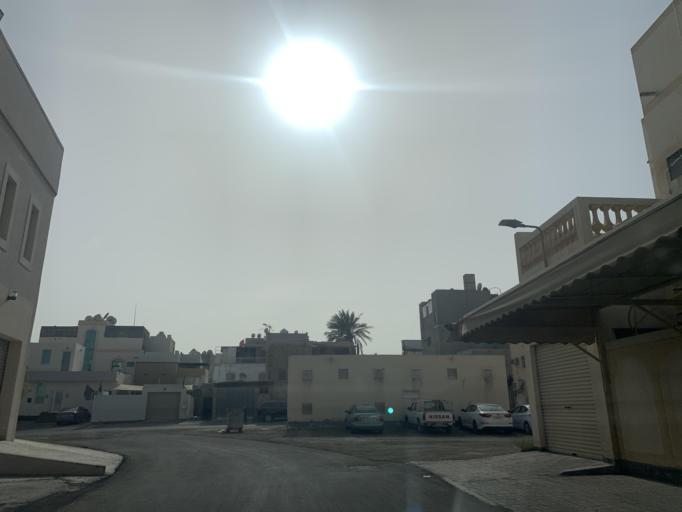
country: BH
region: Northern
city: Madinat `Isa
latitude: 26.1616
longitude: 50.5187
